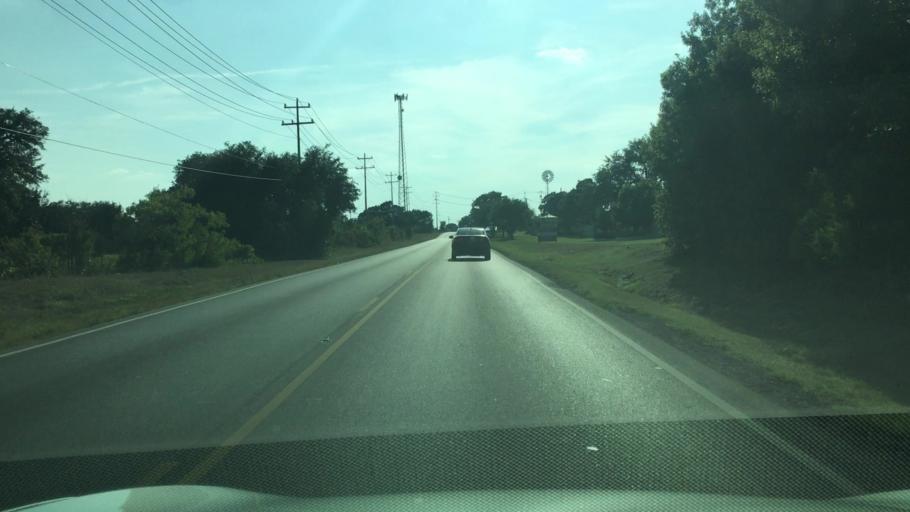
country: US
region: Texas
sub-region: Hays County
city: Dripping Springs
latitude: 30.1172
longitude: -97.9817
